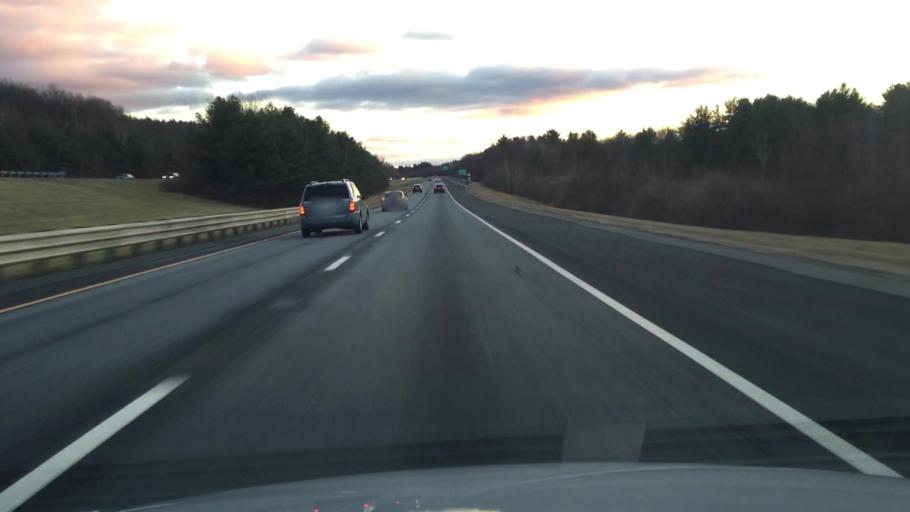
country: US
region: Massachusetts
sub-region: Worcester County
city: West Boylston
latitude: 42.3593
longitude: -71.8137
